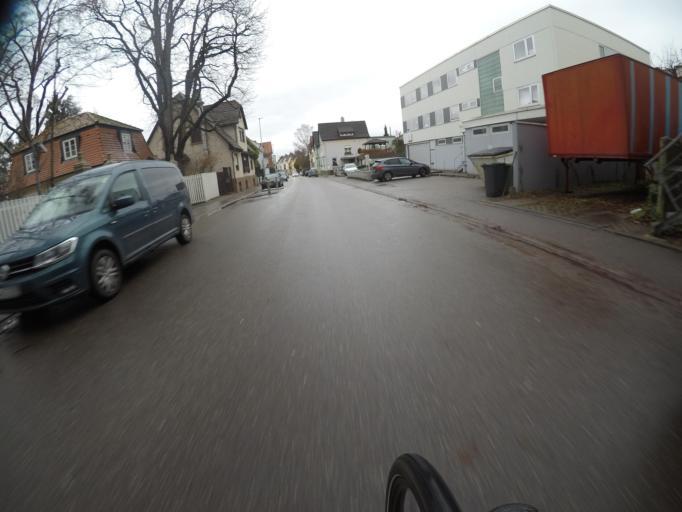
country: DE
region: Baden-Wuerttemberg
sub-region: Regierungsbezirk Stuttgart
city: Bietigheim-Bissingen
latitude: 48.9573
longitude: 9.1234
